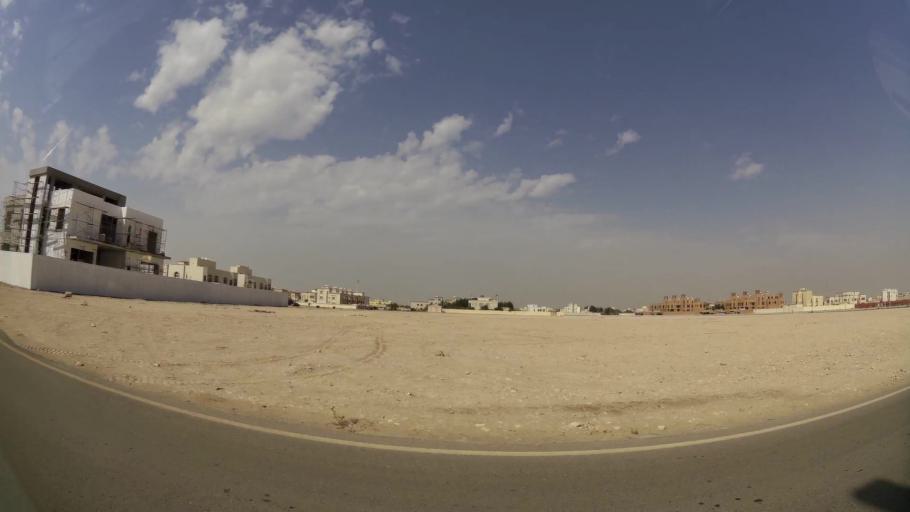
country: AE
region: Abu Dhabi
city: Abu Dhabi
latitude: 24.3325
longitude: 54.5663
